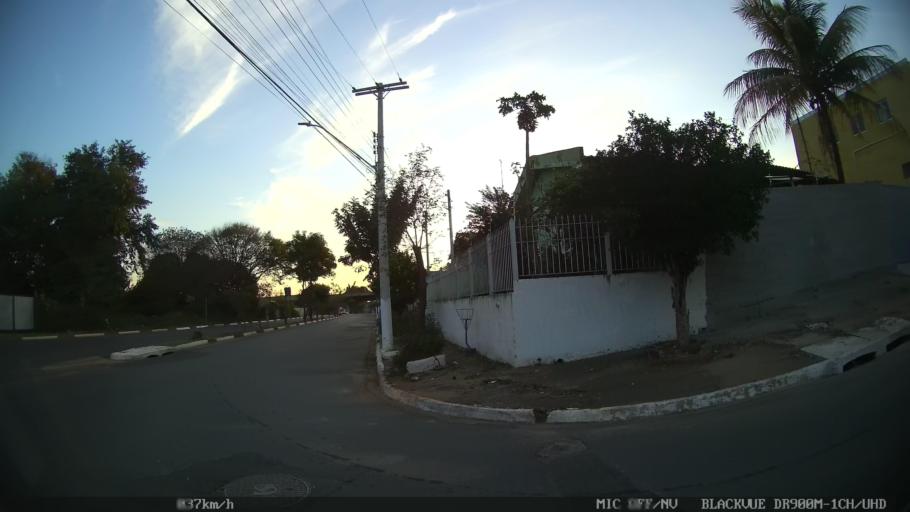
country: BR
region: Sao Paulo
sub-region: Hortolandia
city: Hortolandia
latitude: -22.8595
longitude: -47.2147
